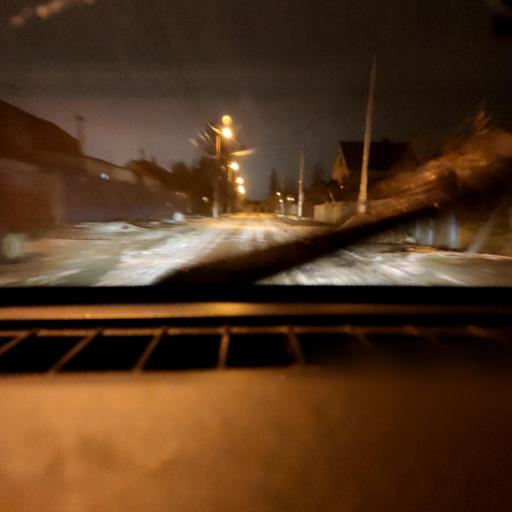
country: RU
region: Voronezj
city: Podgornoye
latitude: 51.7329
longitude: 39.1544
